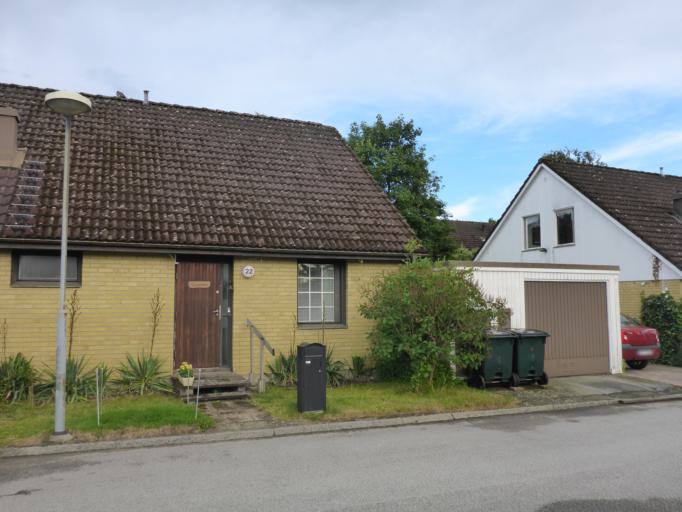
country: SE
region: Skane
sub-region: Lunds Kommun
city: Lund
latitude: 55.7009
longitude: 13.2405
